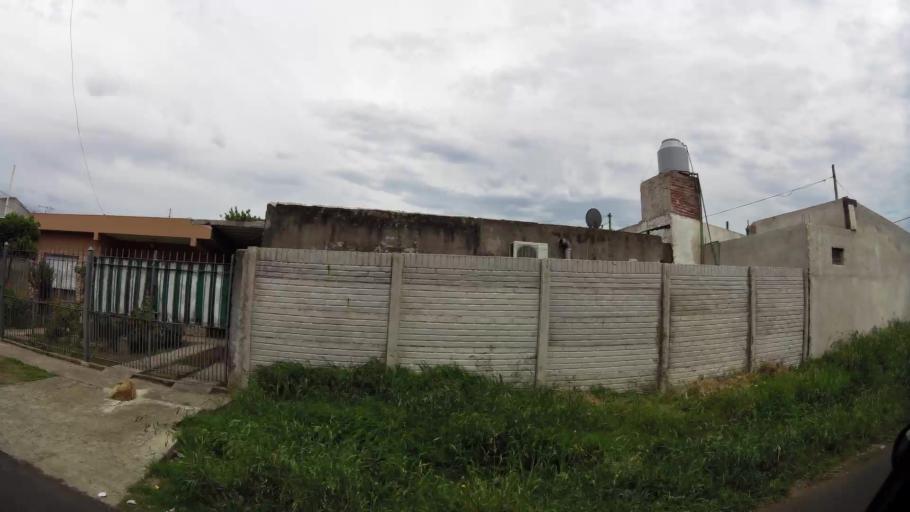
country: AR
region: Buenos Aires
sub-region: Partido de Quilmes
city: Quilmes
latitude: -34.7512
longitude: -58.2062
